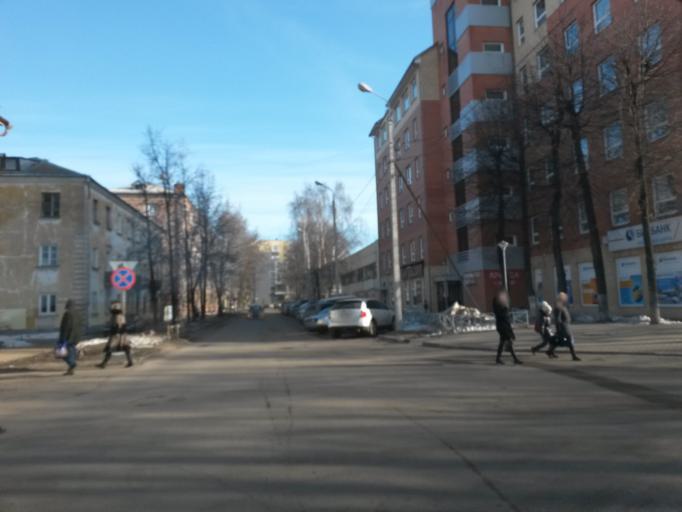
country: RU
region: Jaroslavl
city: Yaroslavl
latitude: 57.6284
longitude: 39.8540
